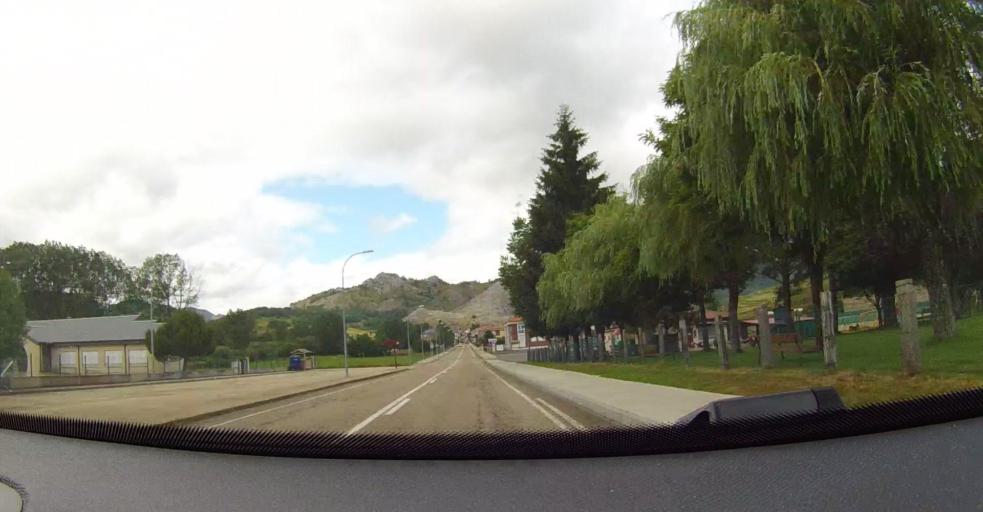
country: ES
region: Castille and Leon
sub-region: Provincia de Leon
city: Puebla de Lillo
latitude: 43.0036
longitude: -5.2677
